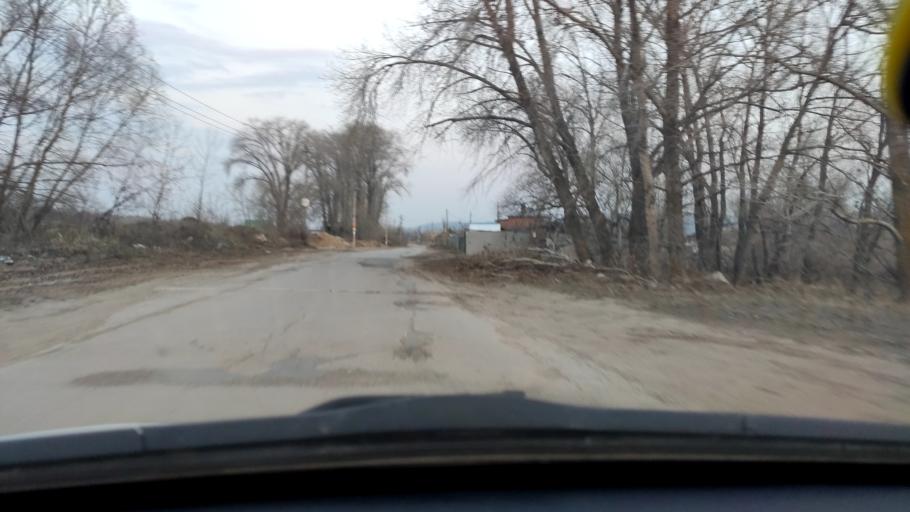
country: RU
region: Samara
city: Zhigulevsk
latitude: 53.4575
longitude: 49.5145
